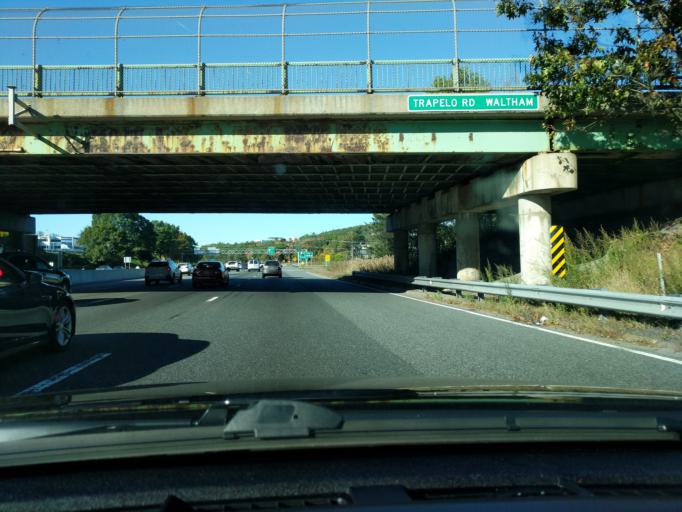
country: US
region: Massachusetts
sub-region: Middlesex County
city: Waltham
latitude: 42.4150
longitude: -71.2571
